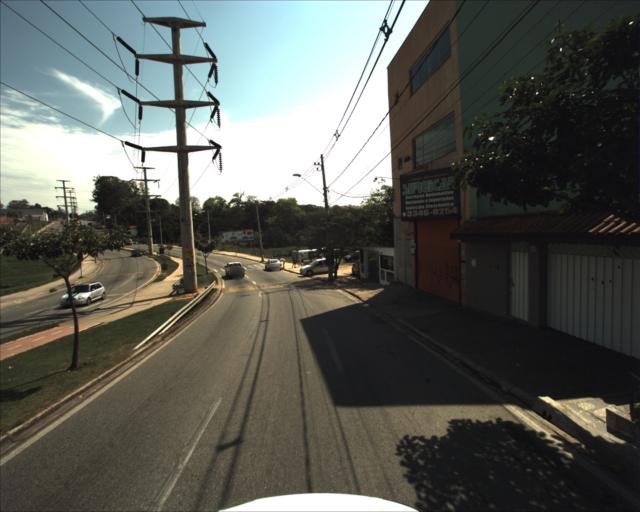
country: BR
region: Sao Paulo
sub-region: Sorocaba
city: Sorocaba
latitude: -23.4449
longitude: -47.4931
